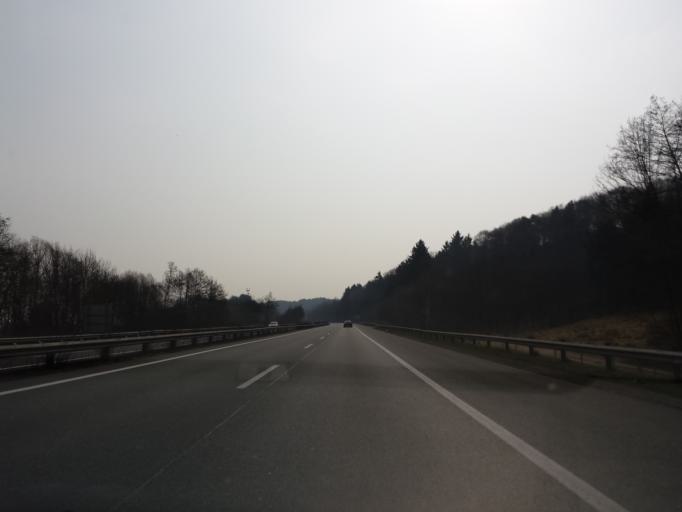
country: AT
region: Styria
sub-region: Politischer Bezirk Weiz
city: Sinabelkirchen
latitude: 47.0939
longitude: 15.8298
